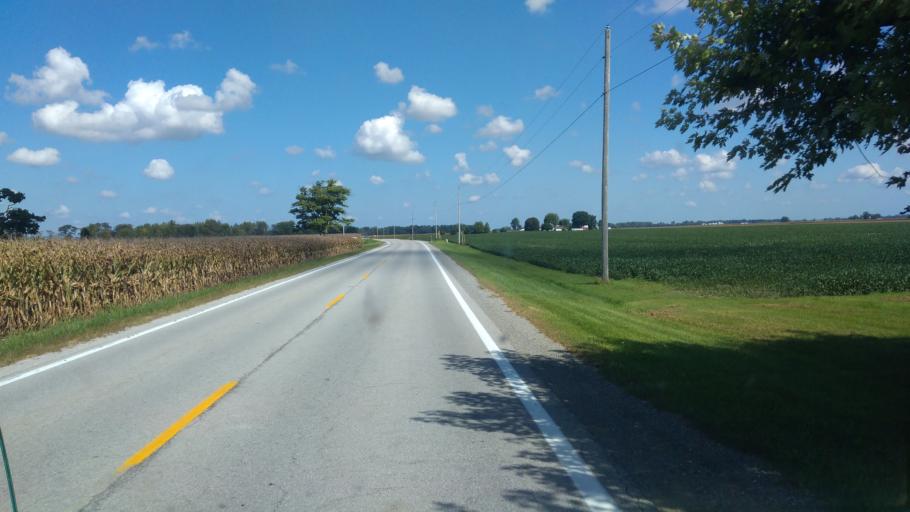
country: US
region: Ohio
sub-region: Marion County
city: Marion
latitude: 40.6623
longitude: -83.1449
